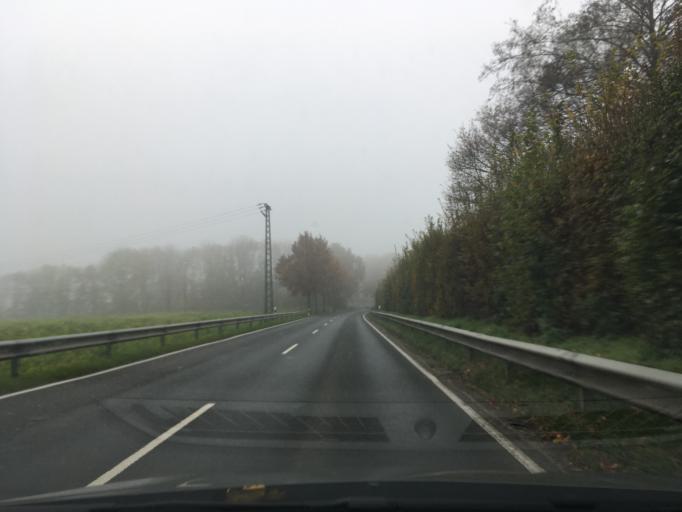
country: DE
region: North Rhine-Westphalia
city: Stadtlohn
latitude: 52.0699
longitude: 6.9273
